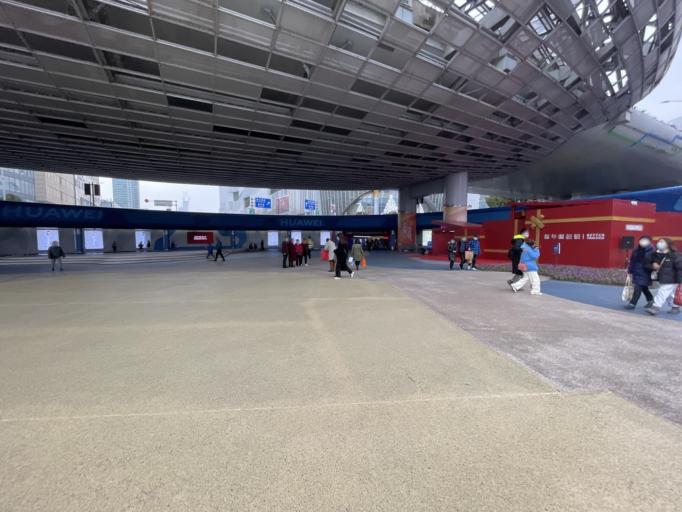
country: CN
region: Shanghai Shi
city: Yangpu
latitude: 31.3018
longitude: 121.5113
